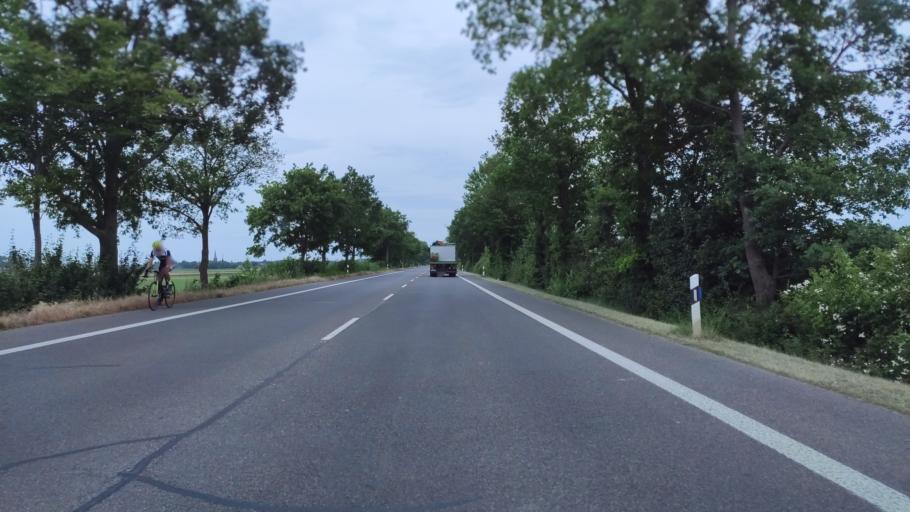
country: DE
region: North Rhine-Westphalia
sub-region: Regierungsbezirk Dusseldorf
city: Kaarst
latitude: 51.1823
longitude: 6.5818
